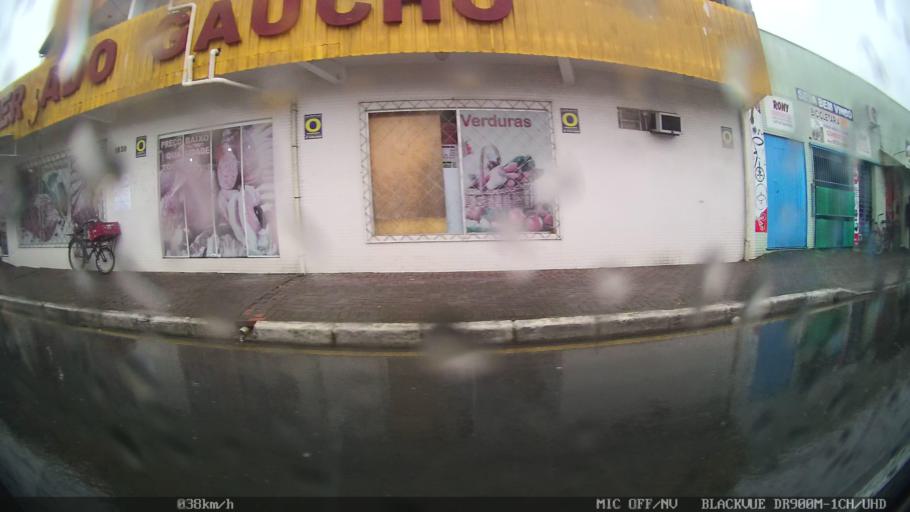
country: BR
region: Santa Catarina
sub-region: Balneario Camboriu
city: Balneario Camboriu
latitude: -27.0030
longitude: -48.6415
